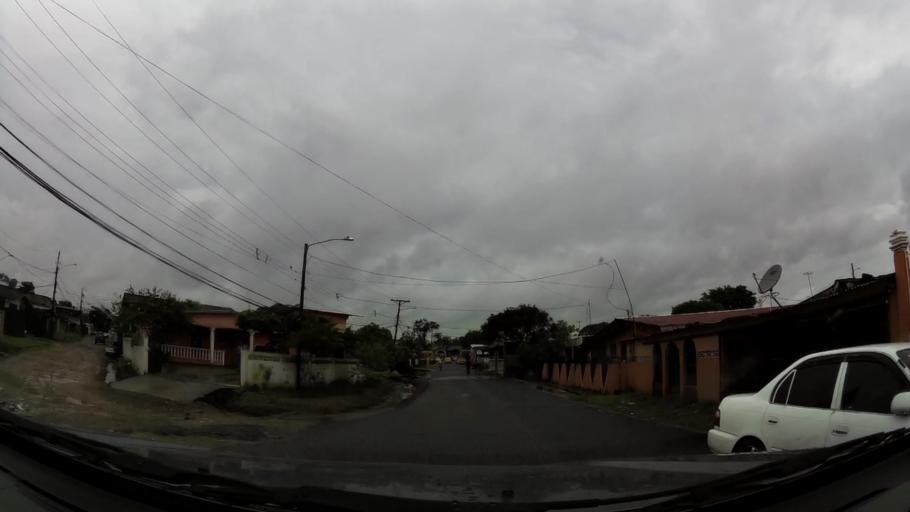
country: PA
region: Colon
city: Arco Iris
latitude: 9.3360
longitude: -79.8768
